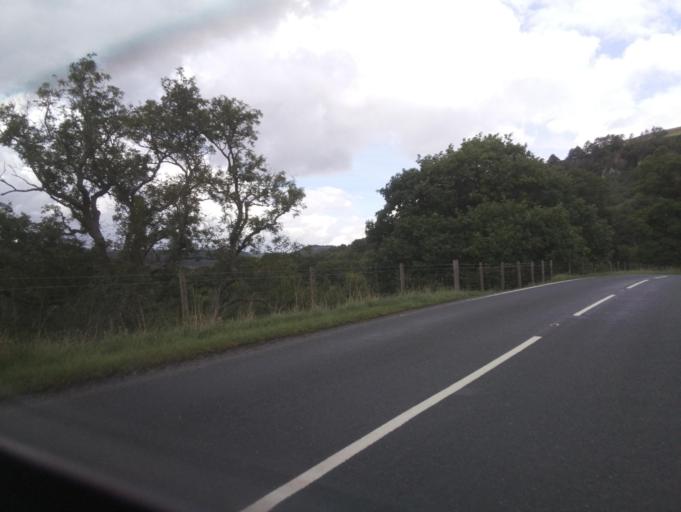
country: GB
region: England
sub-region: North Yorkshire
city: Leyburn
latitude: 54.3861
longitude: -1.8285
